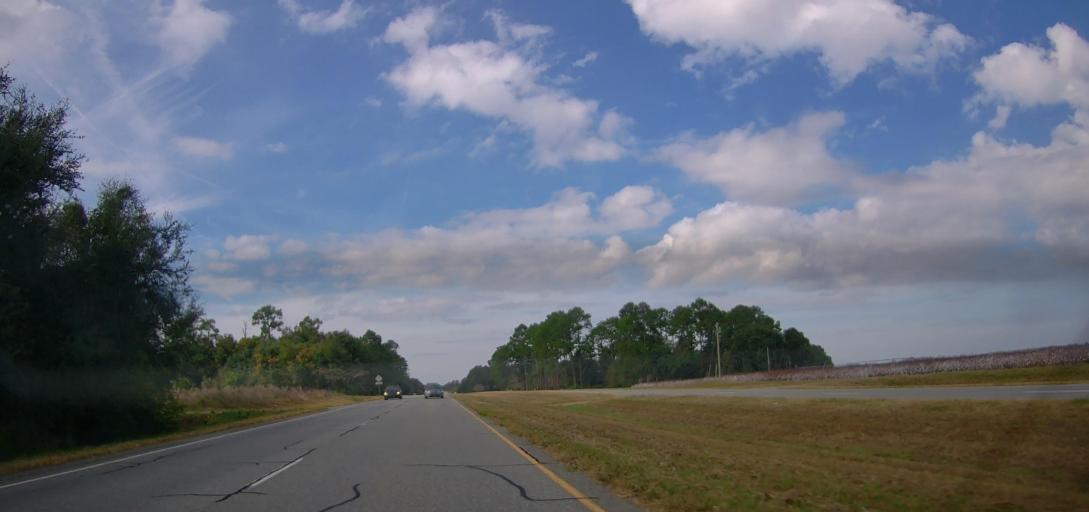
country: US
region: Georgia
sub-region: Mitchell County
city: Camilla
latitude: 31.2007
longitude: -84.1696
